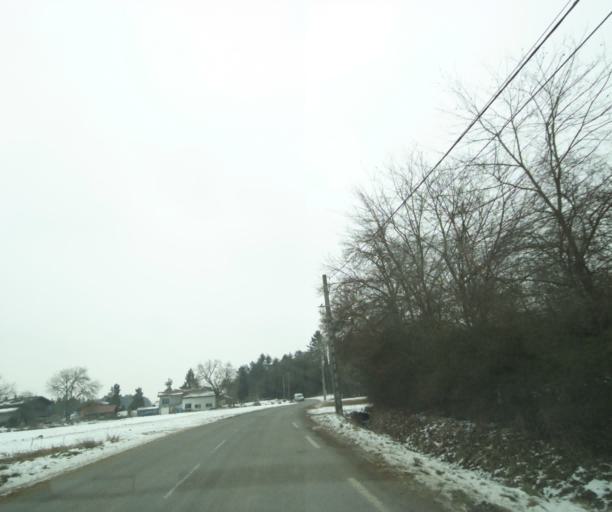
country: FR
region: Rhone-Alpes
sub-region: Departement de la Haute-Savoie
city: Reignier-Esery
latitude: 46.1249
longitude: 6.2824
